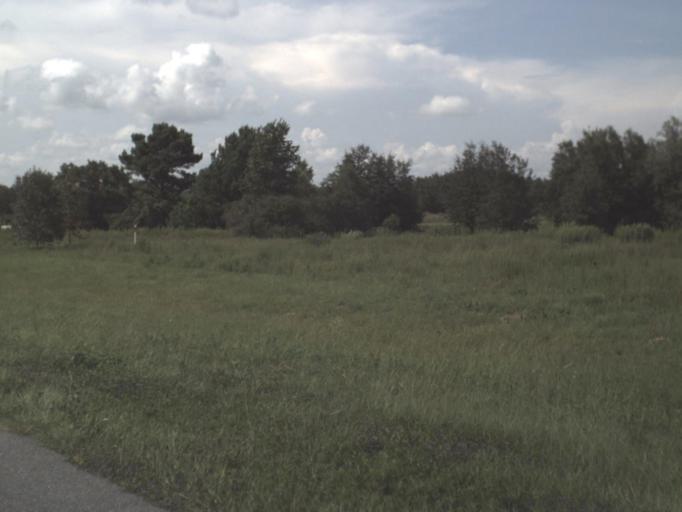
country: US
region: Florida
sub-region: Citrus County
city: Citrus Springs
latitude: 28.9758
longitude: -82.4256
